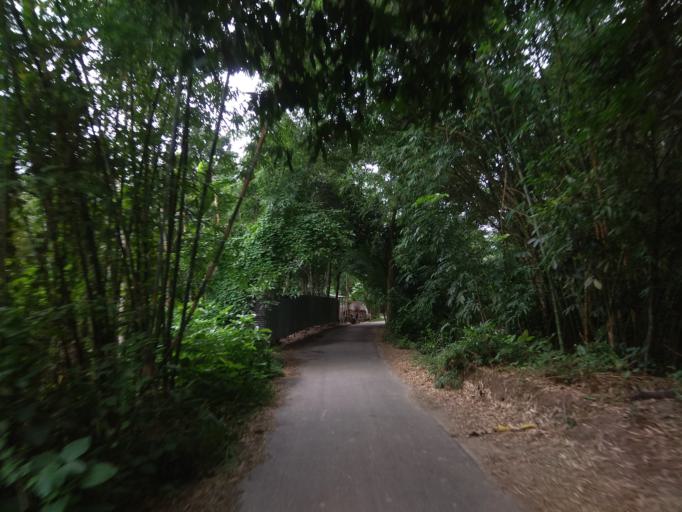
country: BD
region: Dhaka
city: Dohar
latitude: 23.4883
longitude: 89.9942
